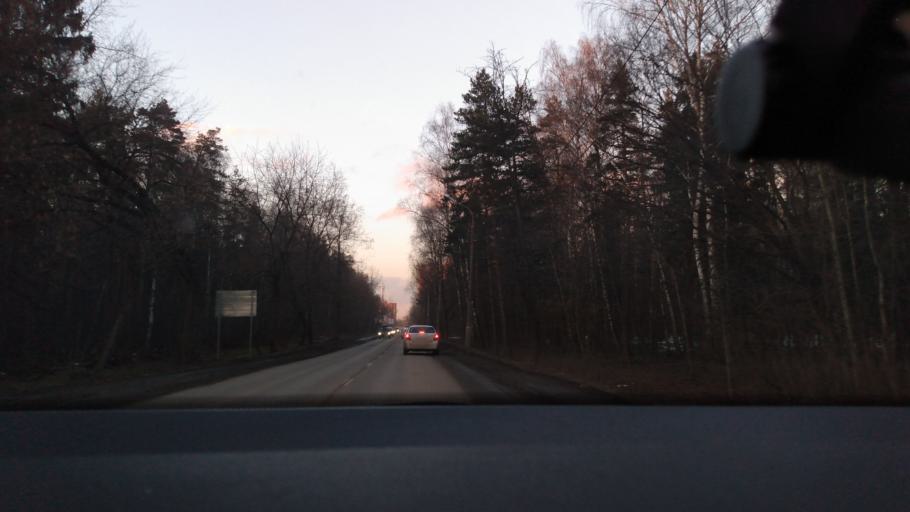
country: RU
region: Moskovskaya
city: Saltykovka
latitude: 55.7857
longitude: 37.9316
